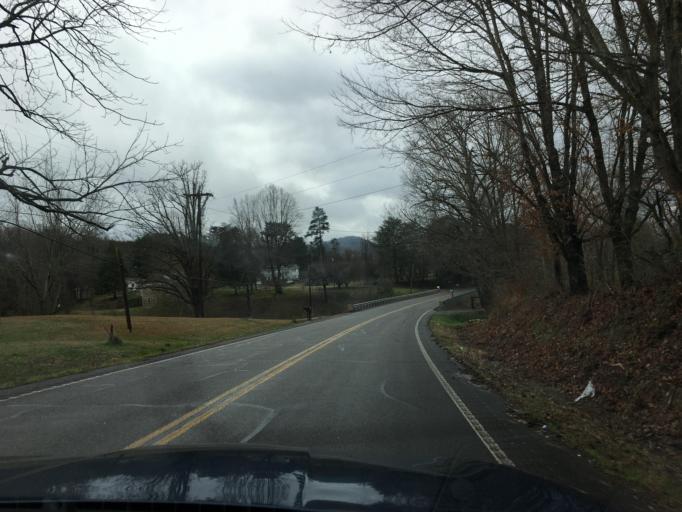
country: US
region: Tennessee
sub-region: Polk County
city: Benton
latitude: 35.1345
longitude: -84.6433
